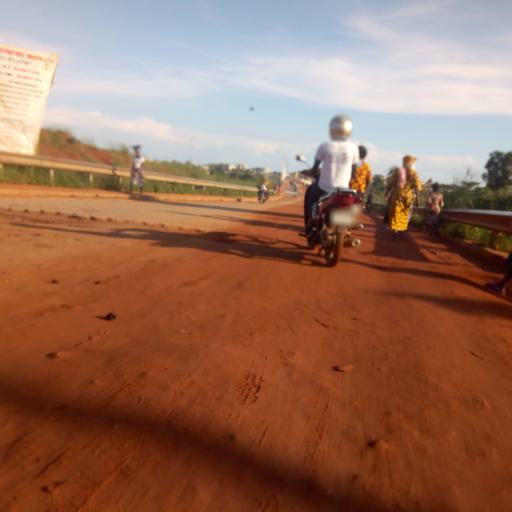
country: BJ
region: Atlantique
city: Hevie
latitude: 6.3984
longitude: 2.2693
